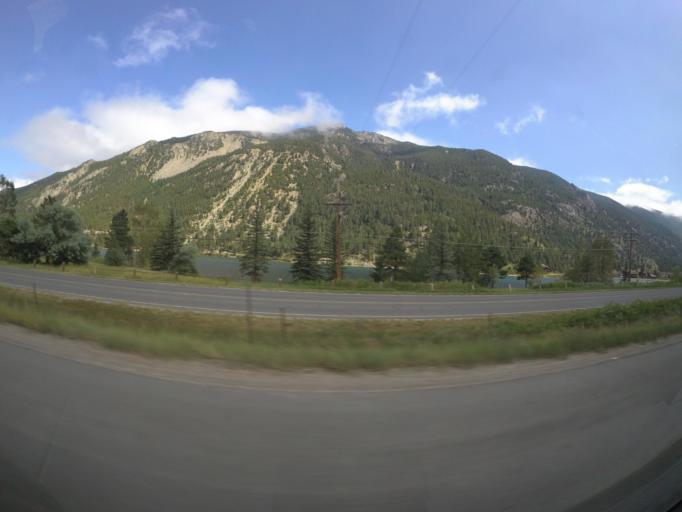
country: US
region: Colorado
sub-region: Clear Creek County
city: Georgetown
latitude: 39.7287
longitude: -105.6944
